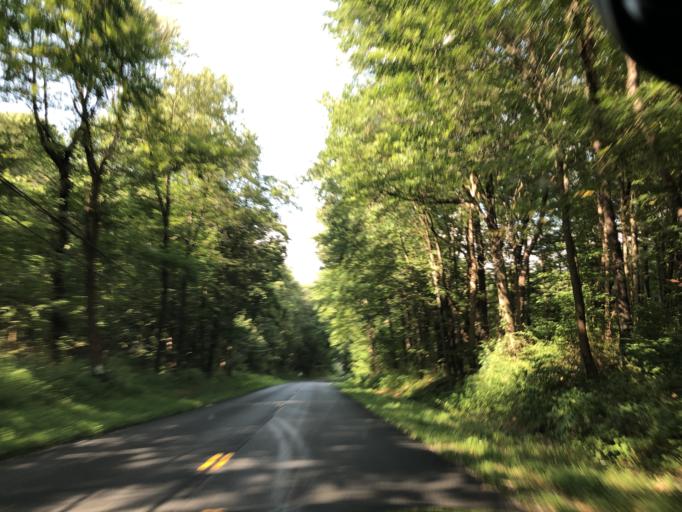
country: US
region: Maryland
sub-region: Carroll County
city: Mount Airy
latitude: 39.4066
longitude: -77.1795
